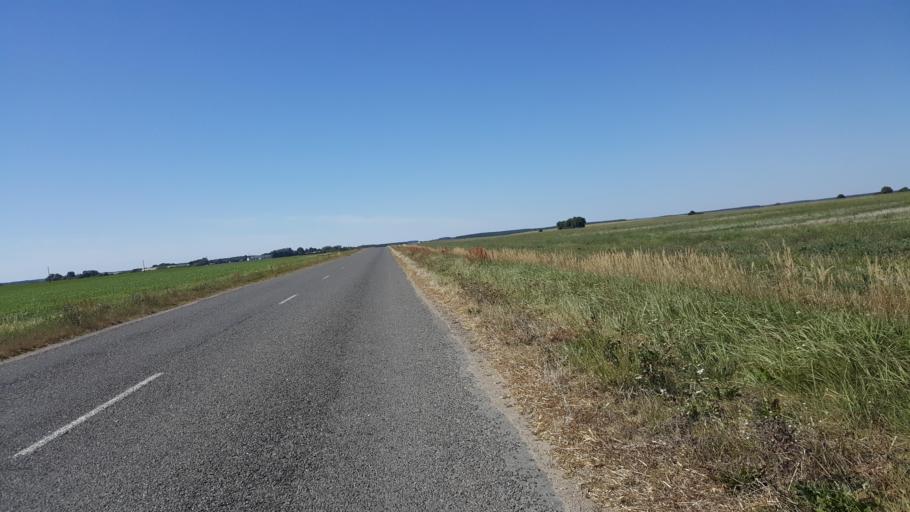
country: PL
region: Lublin Voivodeship
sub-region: Powiat bialski
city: Rokitno
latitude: 52.2275
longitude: 23.3781
